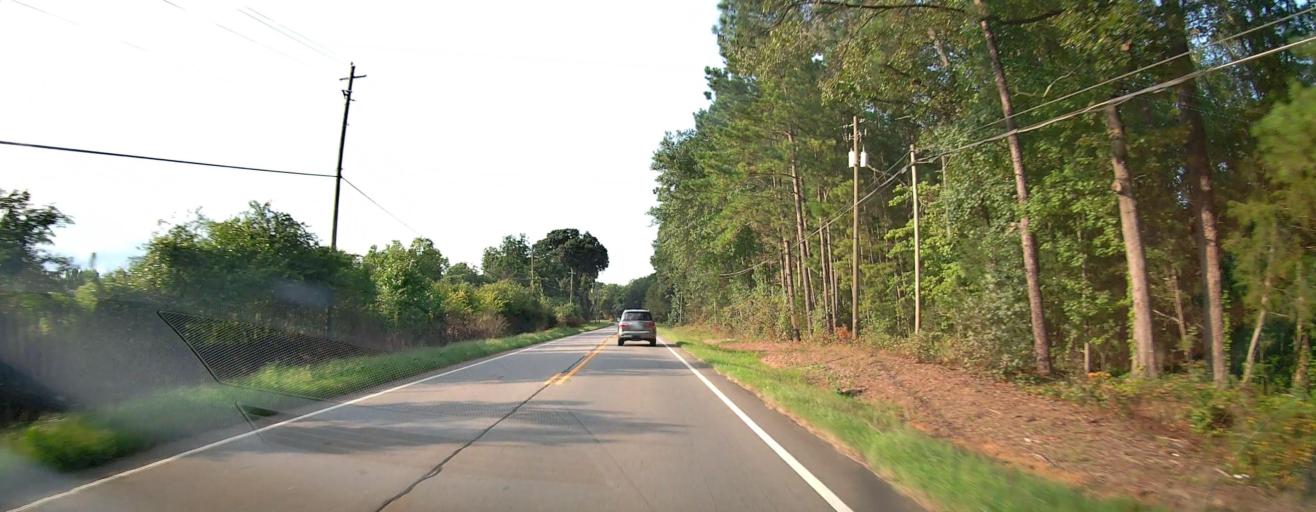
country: US
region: Georgia
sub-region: Monroe County
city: Forsyth
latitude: 33.0223
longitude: -83.9399
